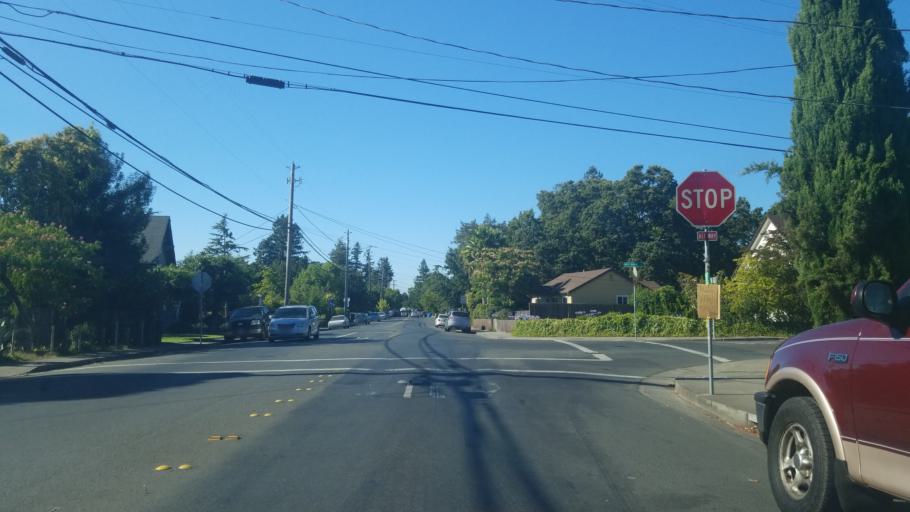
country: US
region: California
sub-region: Sonoma County
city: Roseland
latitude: 38.4255
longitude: -122.7247
